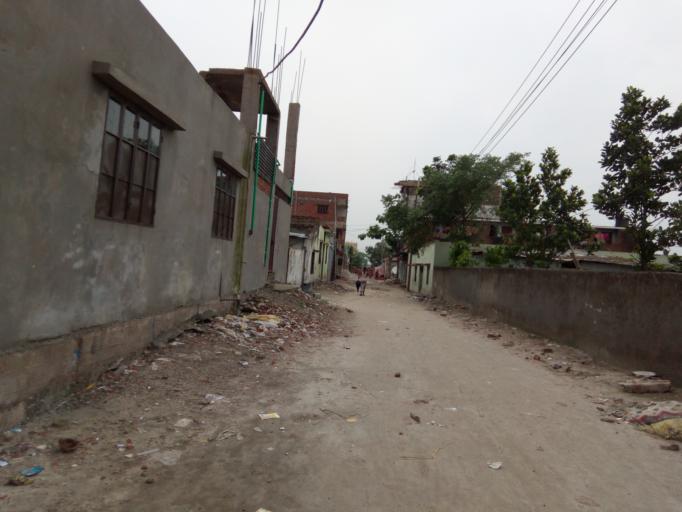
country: BD
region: Dhaka
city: Azimpur
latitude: 23.7673
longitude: 90.3435
